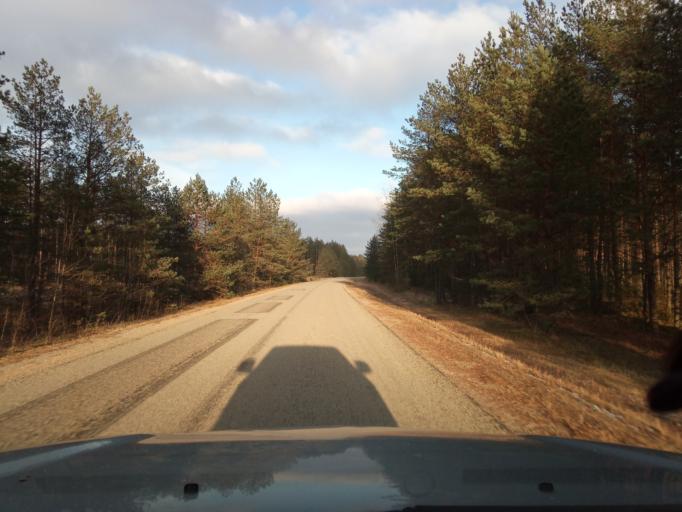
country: LT
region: Alytaus apskritis
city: Varena
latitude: 54.1515
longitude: 24.4831
